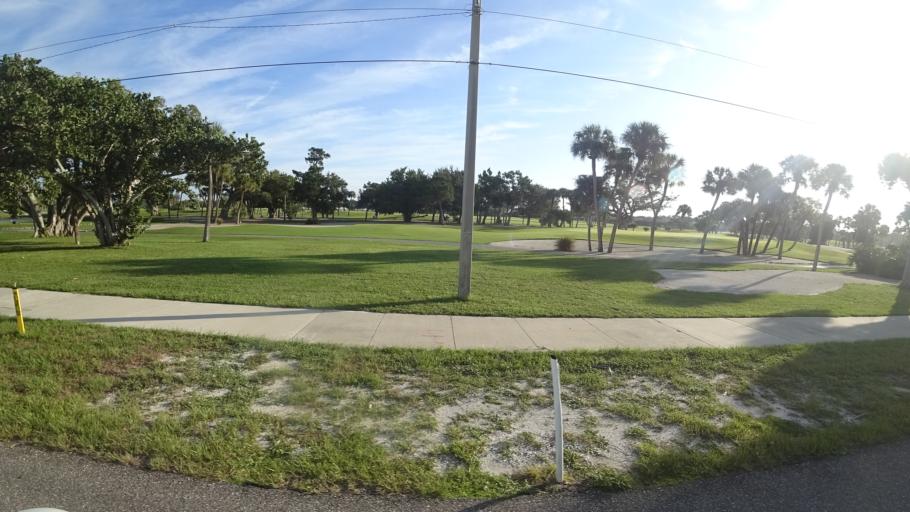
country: US
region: Florida
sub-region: Manatee County
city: Longboat Key
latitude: 27.3645
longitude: -82.6225
